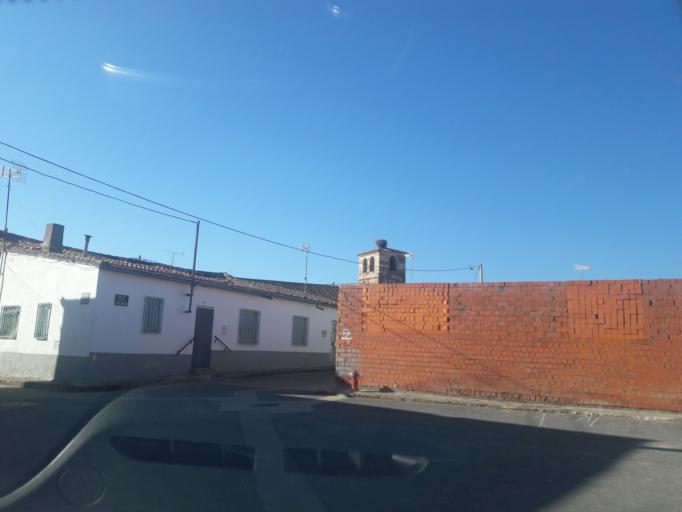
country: ES
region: Castille and Leon
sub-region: Provincia de Salamanca
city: Penarandilla
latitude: 40.8832
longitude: -5.3947
